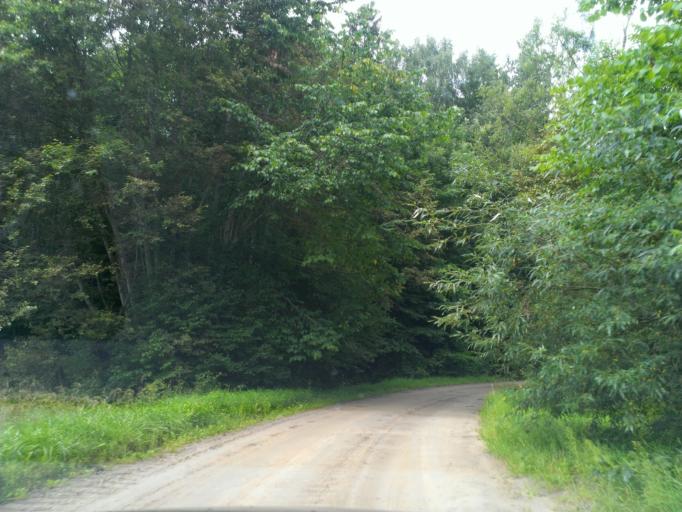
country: LV
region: Ligatne
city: Ligatne
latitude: 57.2119
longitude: 25.0096
